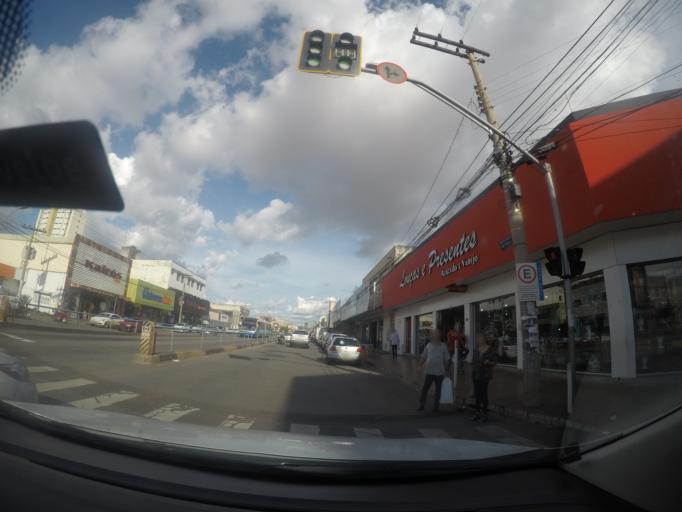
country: BR
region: Goias
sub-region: Goiania
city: Goiania
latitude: -16.6716
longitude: -49.2931
